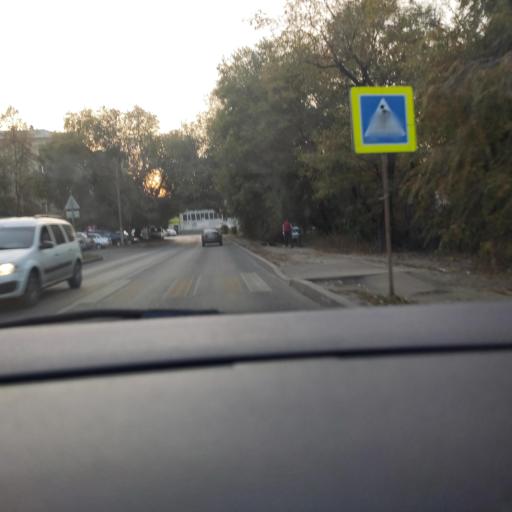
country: RU
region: Voronezj
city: Voronezh
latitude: 51.6887
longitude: 39.1951
